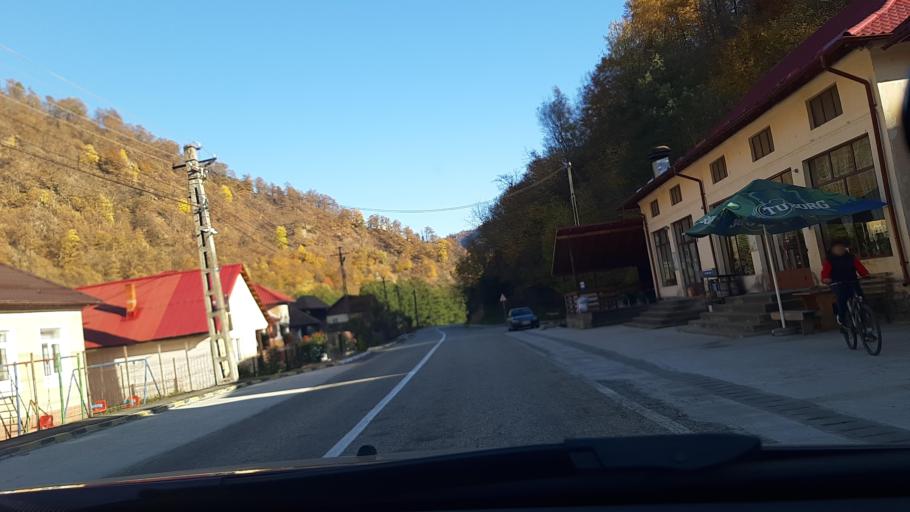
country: RO
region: Valcea
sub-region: Comuna Malaia
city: Malaia
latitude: 45.3535
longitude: 24.1352
